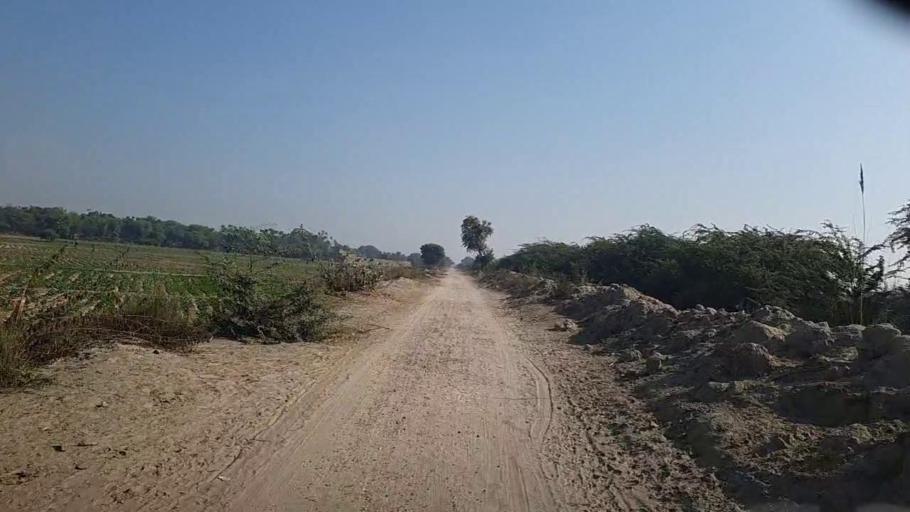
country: PK
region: Sindh
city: Darya Khan Marri
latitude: 26.7081
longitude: 68.3252
